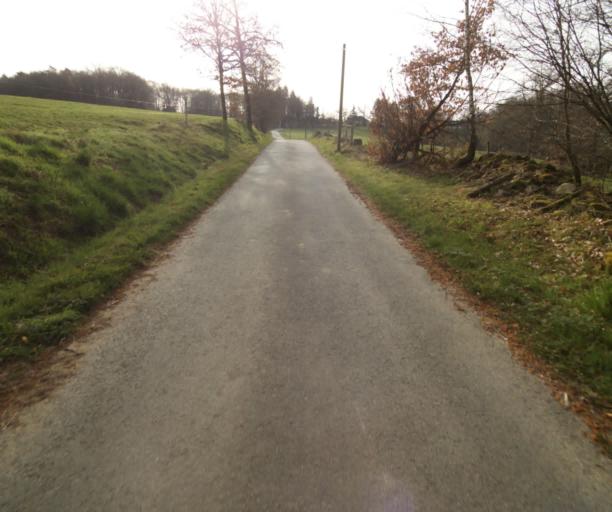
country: FR
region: Limousin
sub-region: Departement de la Correze
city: Chamboulive
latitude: 45.4429
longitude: 1.7550
